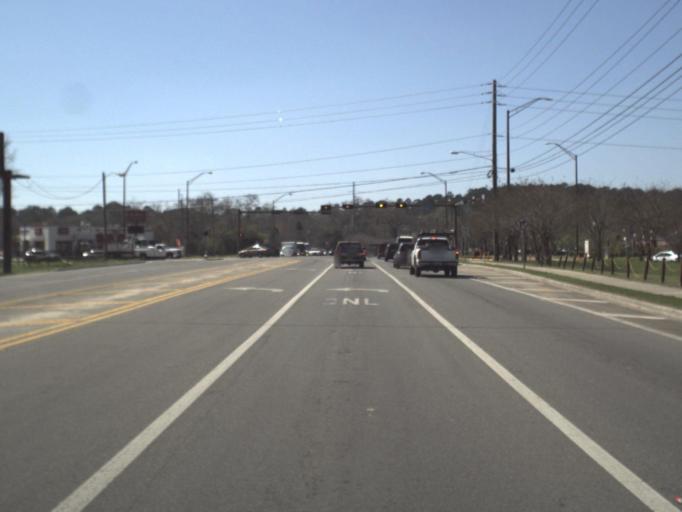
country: US
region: Florida
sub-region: Leon County
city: Tallahassee
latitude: 30.4356
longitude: -84.3005
